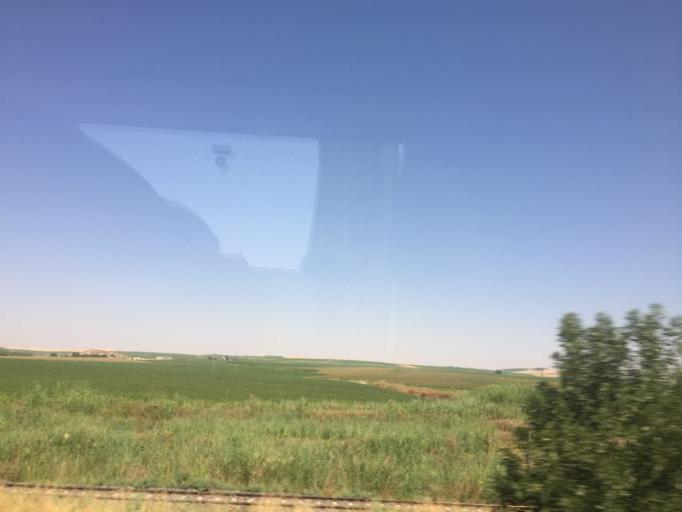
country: TR
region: Diyarbakir
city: Tepe
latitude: 37.8511
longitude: 40.7617
